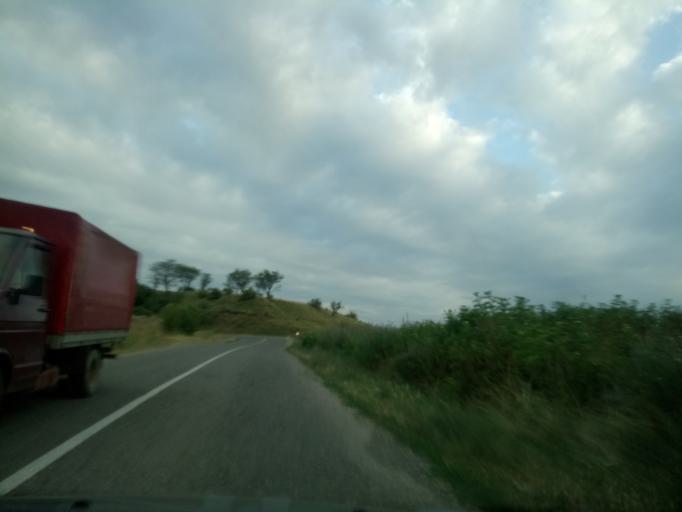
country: RS
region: Autonomna Pokrajina Vojvodina
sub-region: Sremski Okrug
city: Irig
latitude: 45.0937
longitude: 19.8660
